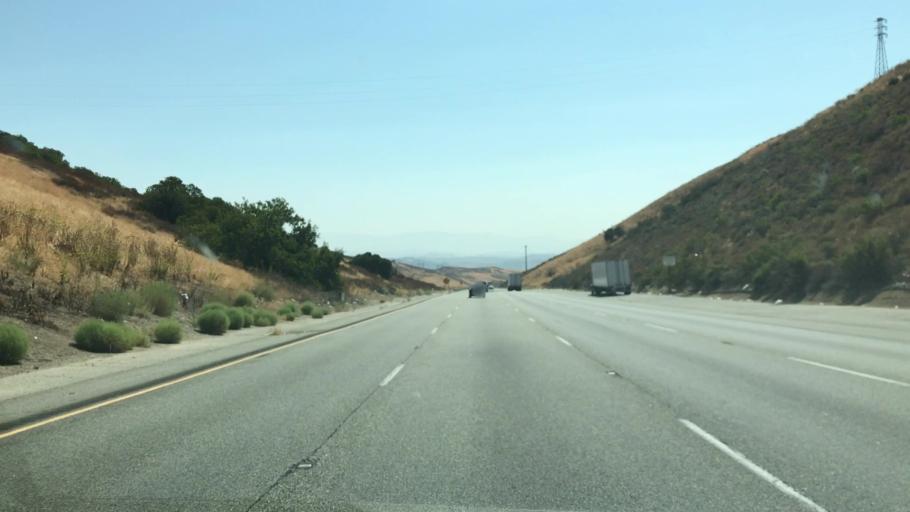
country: US
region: California
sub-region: Los Angeles County
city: Castaic
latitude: 34.5528
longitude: -118.6695
